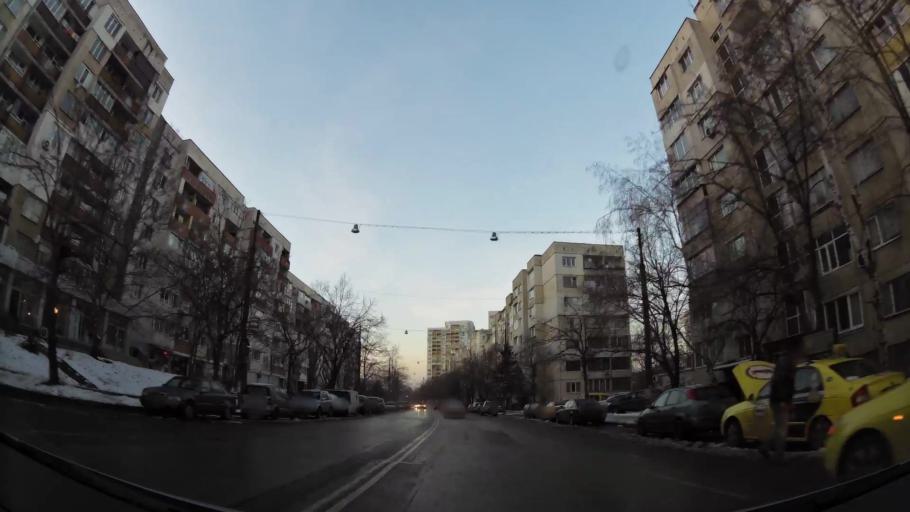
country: BG
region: Sofia-Capital
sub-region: Stolichna Obshtina
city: Sofia
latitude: 42.6873
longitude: 23.3715
